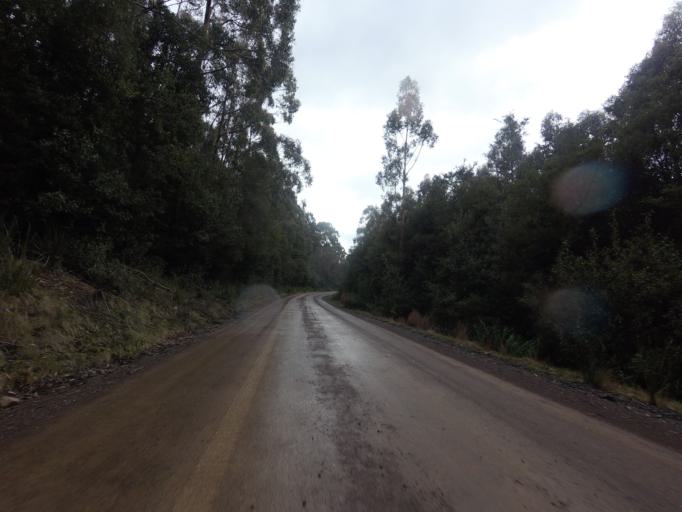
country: AU
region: Tasmania
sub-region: Huon Valley
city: Geeveston
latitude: -43.4778
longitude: 146.8910
